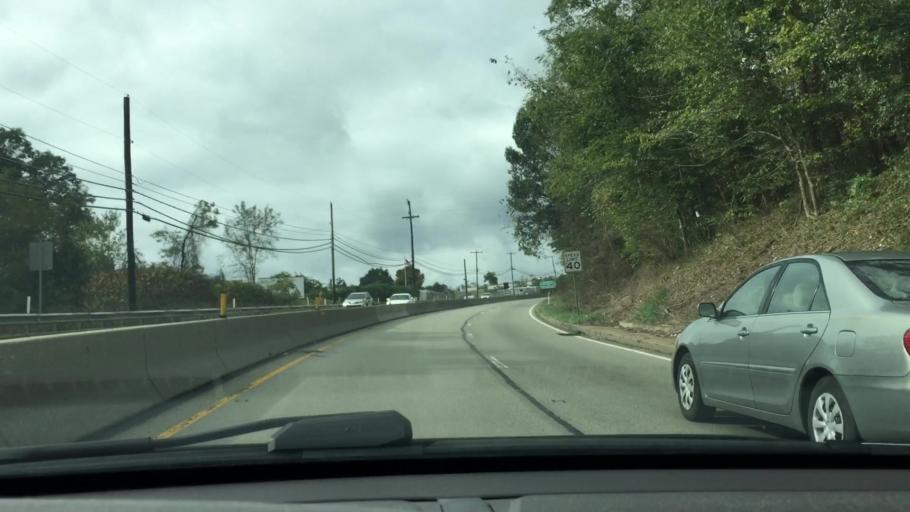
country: US
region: Pennsylvania
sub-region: Allegheny County
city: Elizabeth
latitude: 40.2742
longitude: -79.9019
